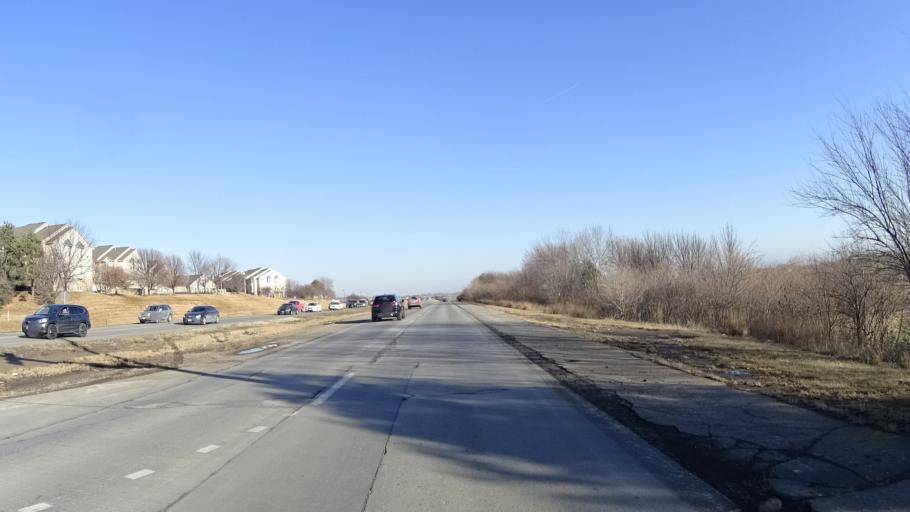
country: US
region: Nebraska
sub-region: Douglas County
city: Bennington
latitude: 41.2920
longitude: -96.1335
